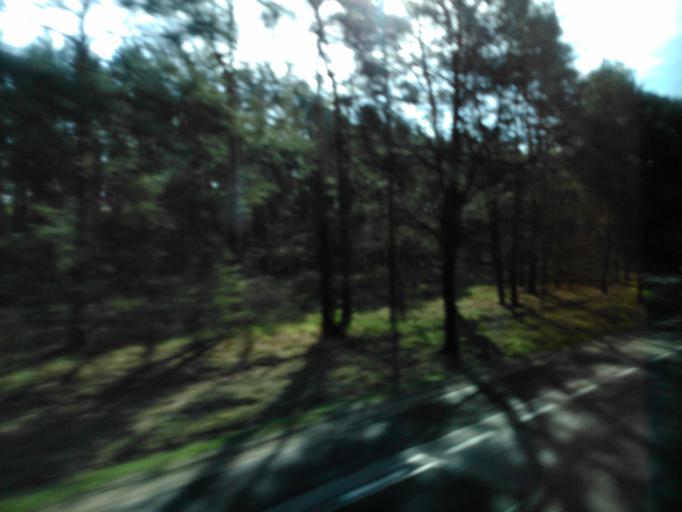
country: PL
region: Kujawsko-Pomorskie
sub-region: Torun
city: Torun
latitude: 52.9805
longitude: 18.6719
